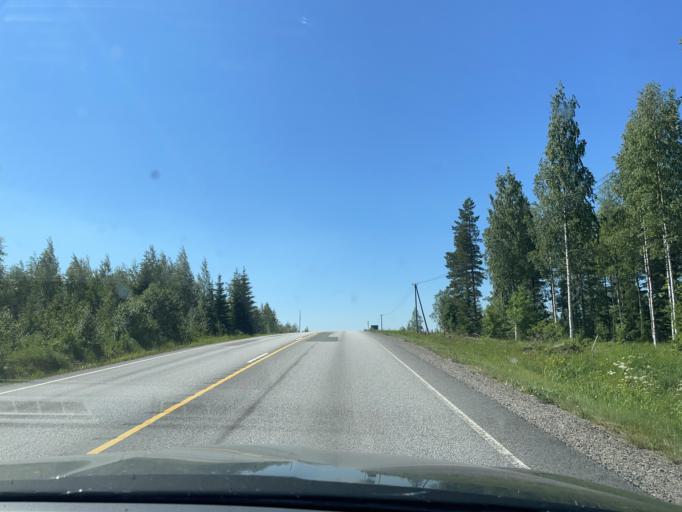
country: FI
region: Central Finland
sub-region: Saarijaervi-Viitasaari
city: Viitasaari
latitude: 63.1461
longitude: 25.8557
